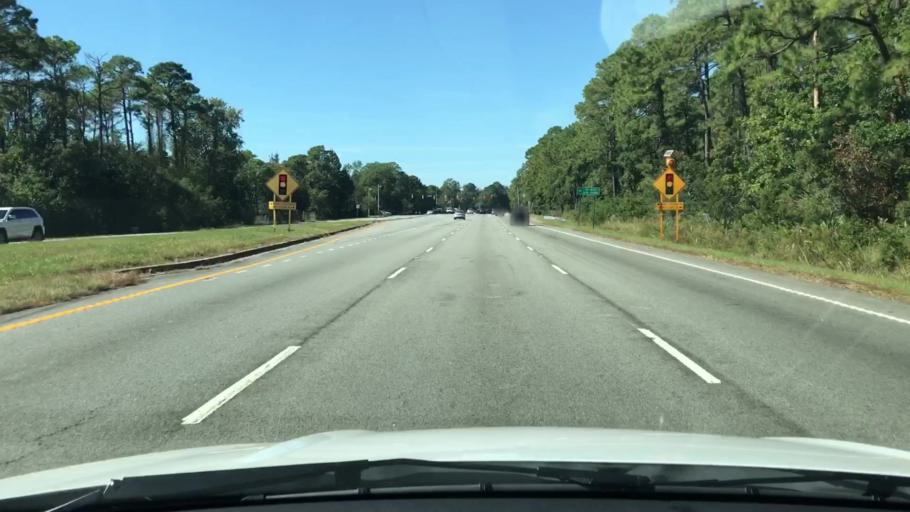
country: US
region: South Carolina
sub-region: Beaufort County
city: Bluffton
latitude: 32.2506
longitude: -80.8398
